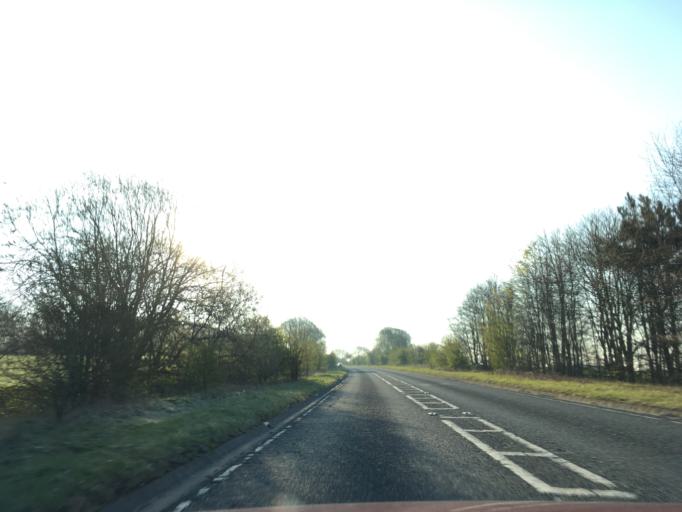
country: GB
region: England
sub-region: Gloucestershire
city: Westfield
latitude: 51.8466
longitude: -1.8781
